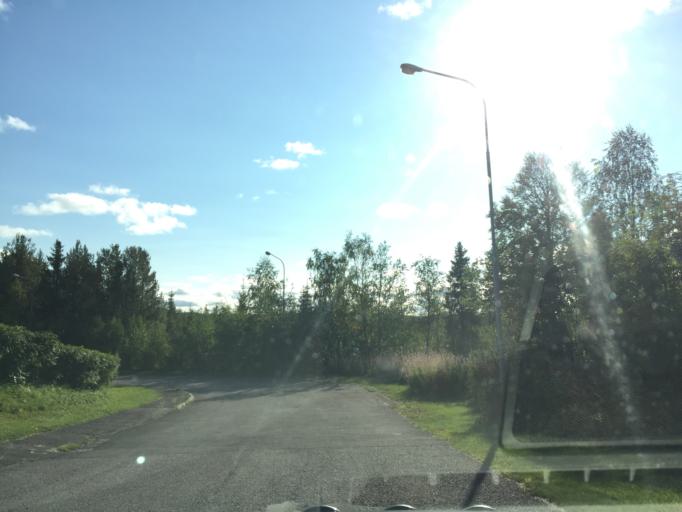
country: SE
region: Norrbotten
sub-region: Gallivare Kommun
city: Malmberget
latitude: 67.6521
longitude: 21.0448
